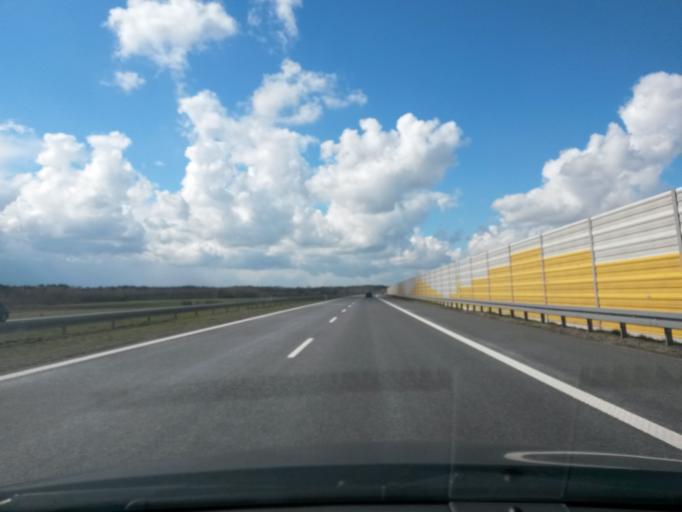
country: PL
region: Lodz Voivodeship
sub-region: Powiat leczycki
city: Swinice Warckie
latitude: 52.0142
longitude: 18.9550
